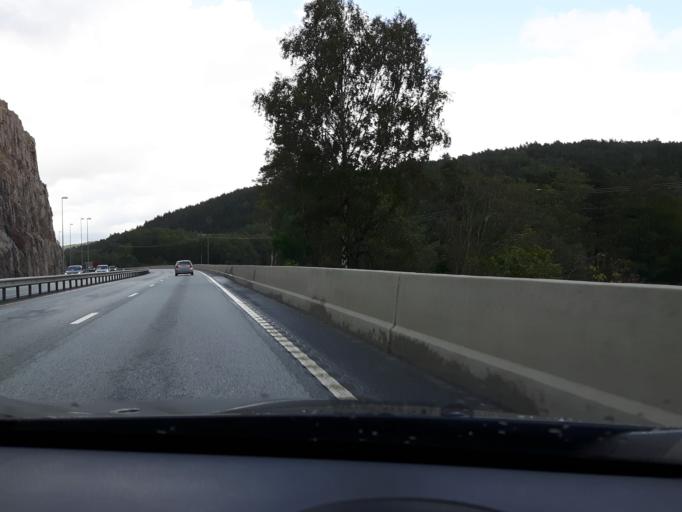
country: NO
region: Vest-Agder
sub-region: Sogne
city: Tangvall
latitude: 58.1070
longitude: 7.8290
